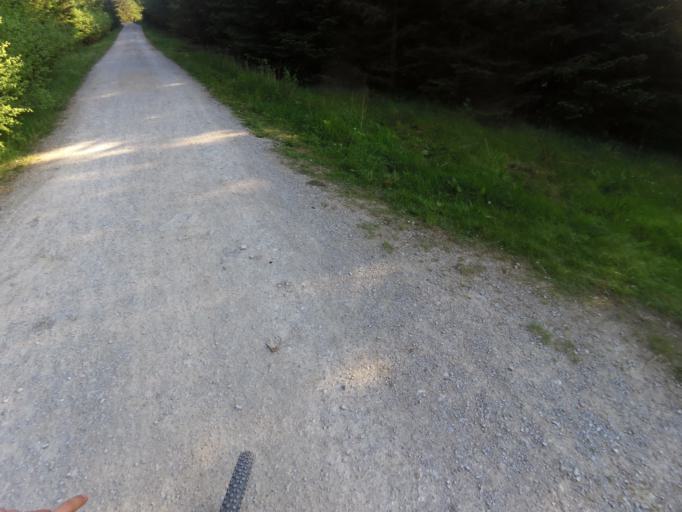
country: GB
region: England
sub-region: North Yorkshire
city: Settle
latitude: 54.0026
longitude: -2.3869
